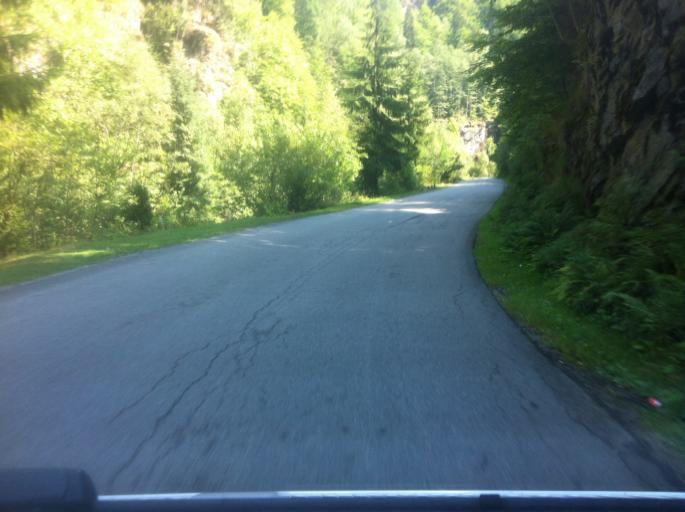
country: RO
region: Hunedoara
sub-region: Oras Petrila
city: Petrila
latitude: 45.4135
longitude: 23.4691
